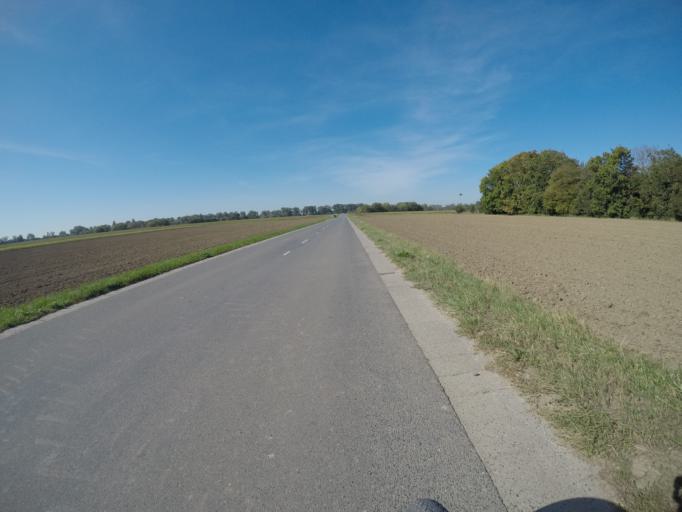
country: DE
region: Hesse
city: Biebesheim
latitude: 49.7791
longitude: 8.4329
